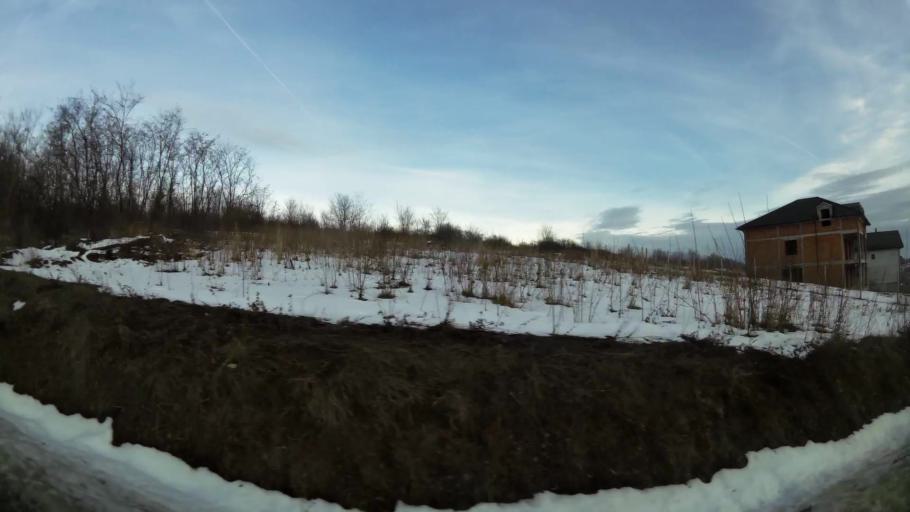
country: RS
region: Central Serbia
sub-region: Belgrade
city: Zvezdara
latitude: 44.7274
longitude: 20.5059
